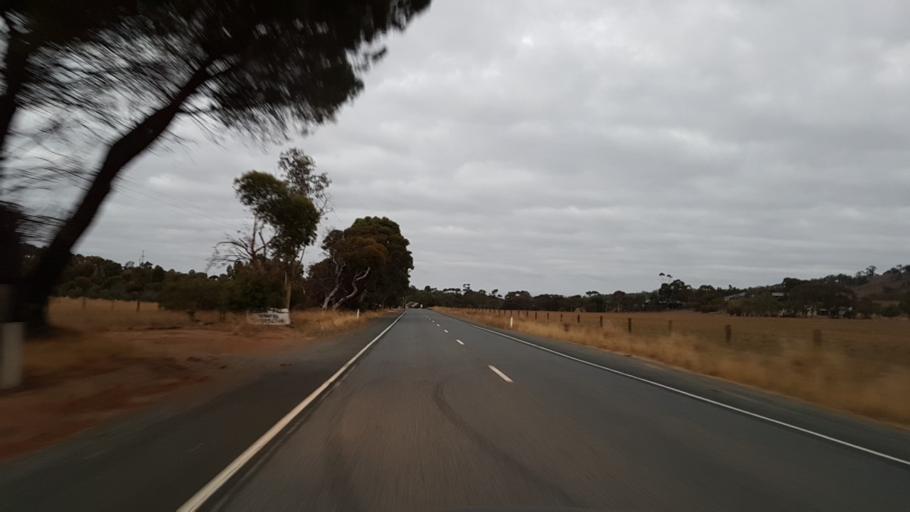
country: AU
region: South Australia
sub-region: Mount Barker
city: Callington
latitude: -35.0634
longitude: 139.0122
